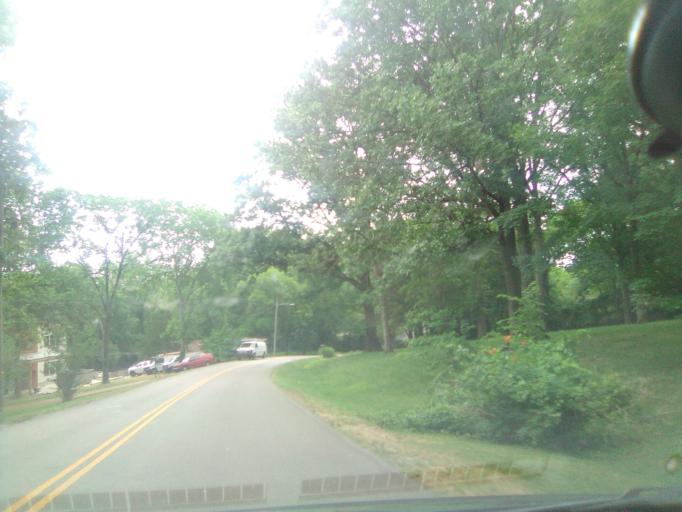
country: US
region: Tennessee
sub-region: Davidson County
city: Belle Meade
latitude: 36.1318
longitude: -86.8758
